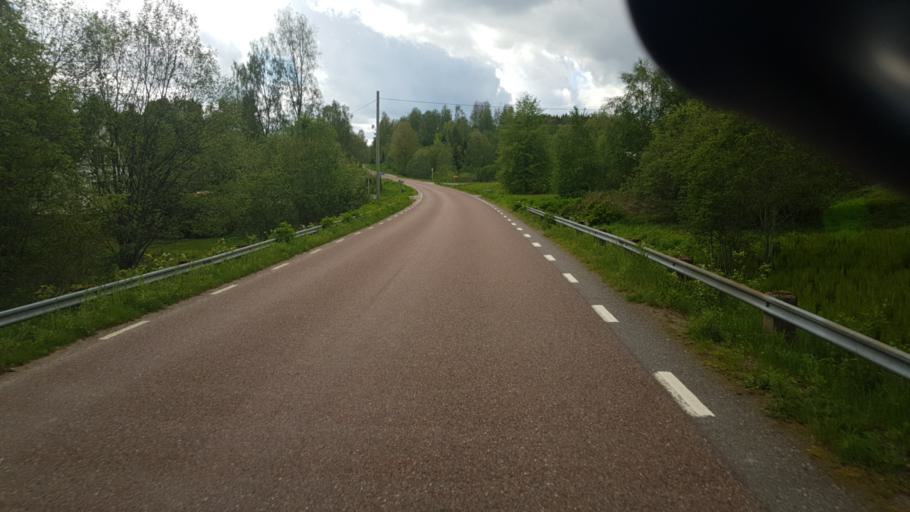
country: NO
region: Hedmark
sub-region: Eidskog
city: Skotterud
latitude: 59.7534
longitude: 12.0534
